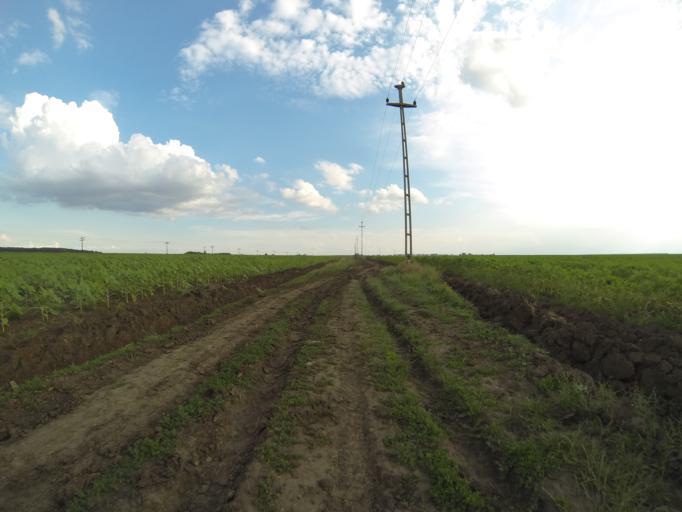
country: RO
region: Dolj
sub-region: Comuna Caloparu
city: Salcuta
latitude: 44.1542
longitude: 23.7048
